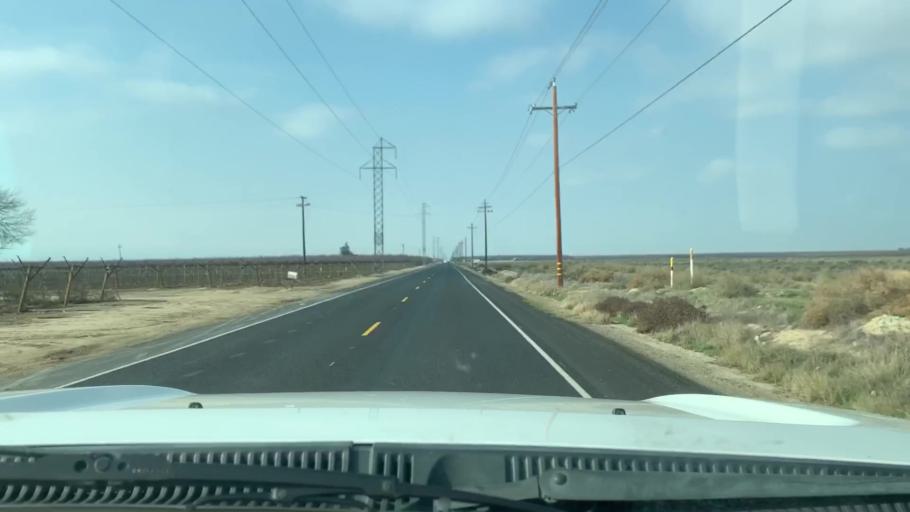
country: US
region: California
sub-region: Kern County
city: Shafter
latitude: 35.4418
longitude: -119.2834
